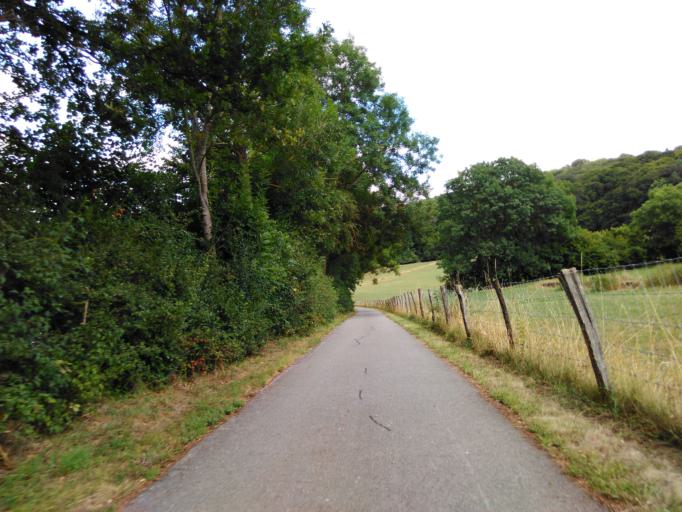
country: DE
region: Rheinland-Pfalz
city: Echternacherbruck
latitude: 49.8108
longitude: 6.4506
